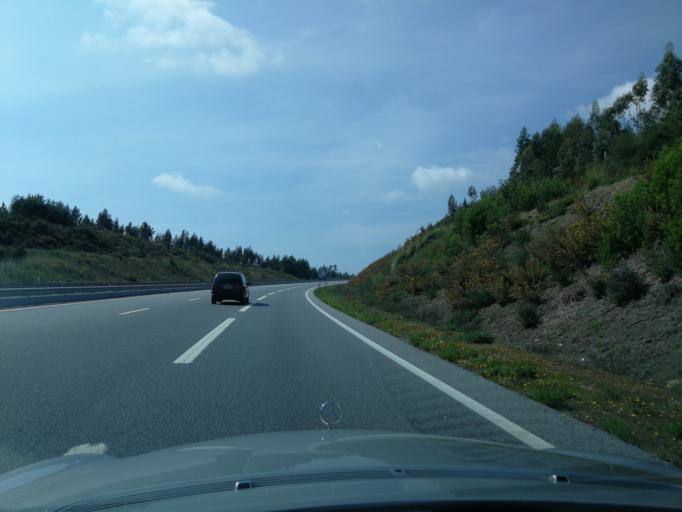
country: PT
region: Braga
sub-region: Vila Nova de Famalicao
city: Ribeirao
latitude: 41.3763
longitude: -8.5634
